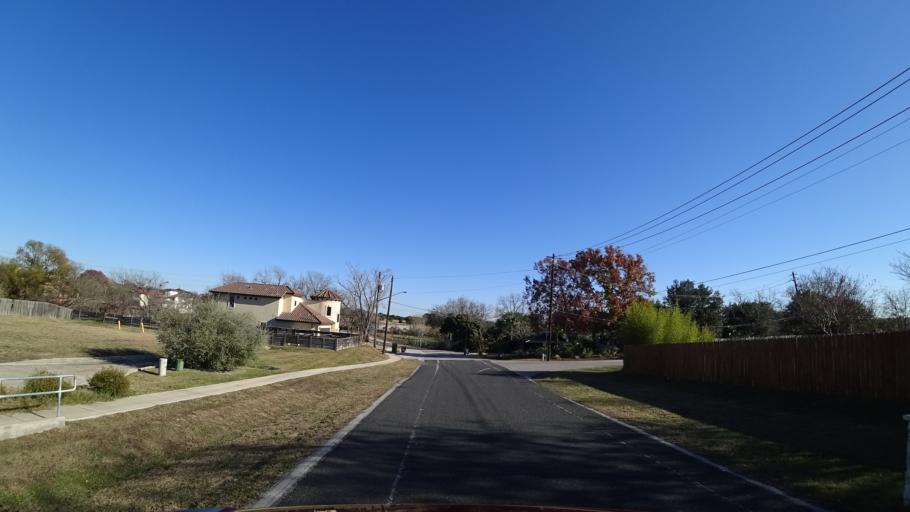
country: US
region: Texas
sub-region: Travis County
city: Wells Branch
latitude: 30.4079
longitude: -97.6922
